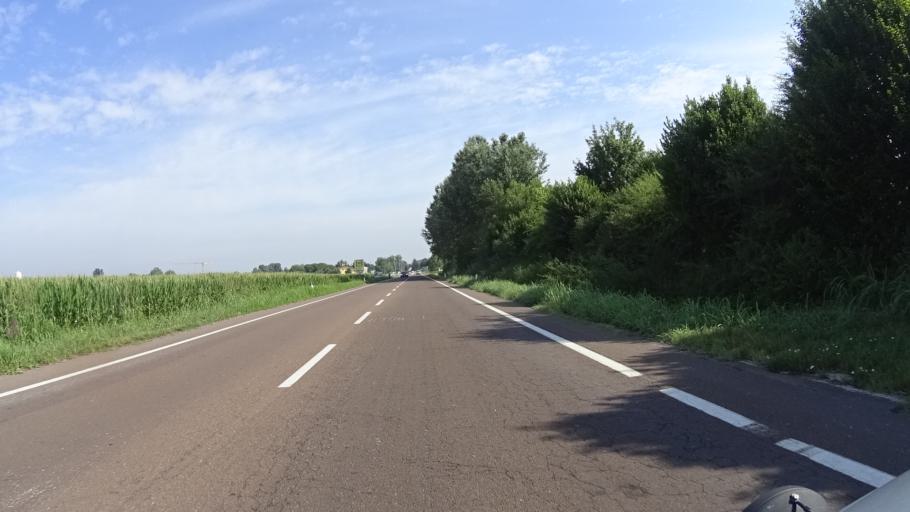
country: IT
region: Veneto
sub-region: Provincia di Venezia
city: San Michele al Tagliamento
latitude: 45.7636
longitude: 12.9854
